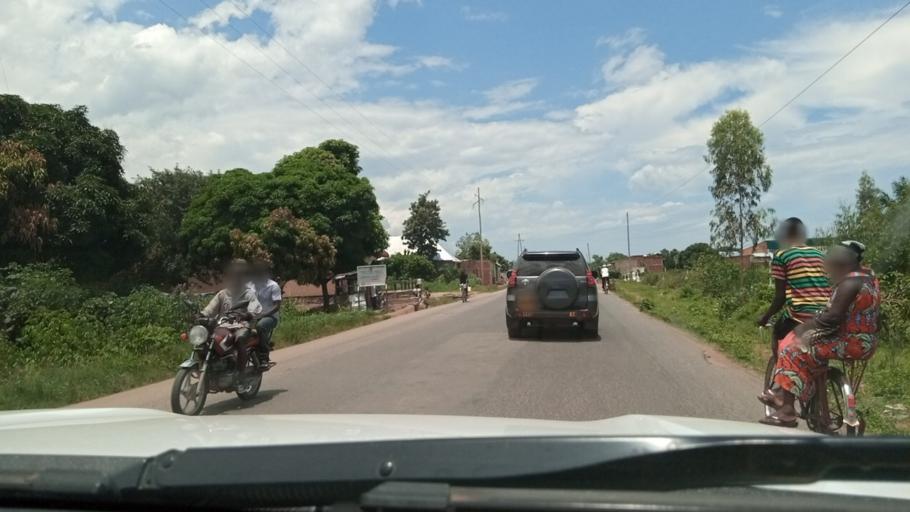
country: BI
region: Bujumbura Mairie
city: Bujumbura
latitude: -3.4646
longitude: 29.3501
